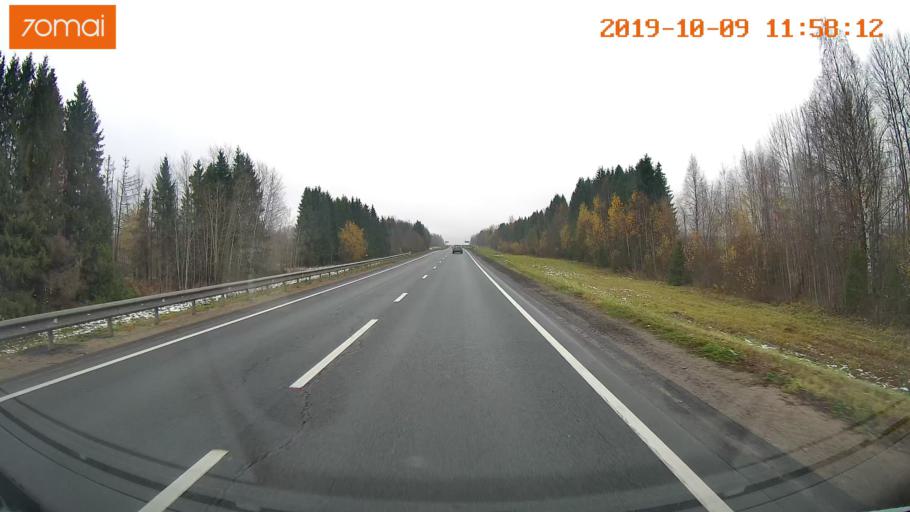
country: RU
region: Vologda
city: Gryazovets
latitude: 58.7215
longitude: 40.2962
